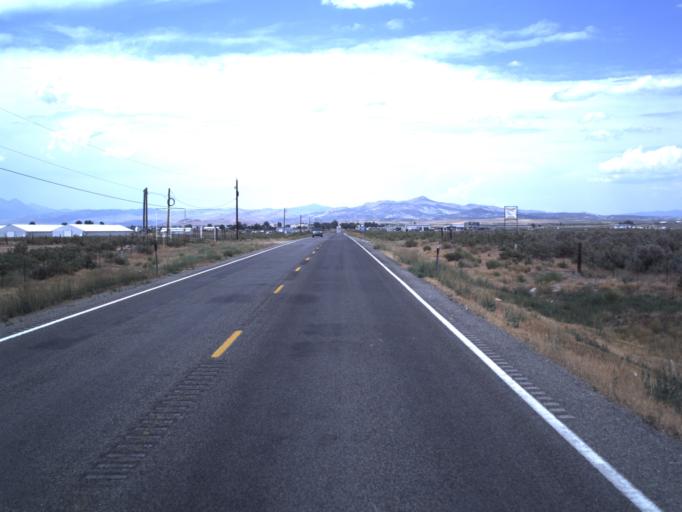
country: US
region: Utah
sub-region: Sanpete County
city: Moroni
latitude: 39.4458
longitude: -111.5624
